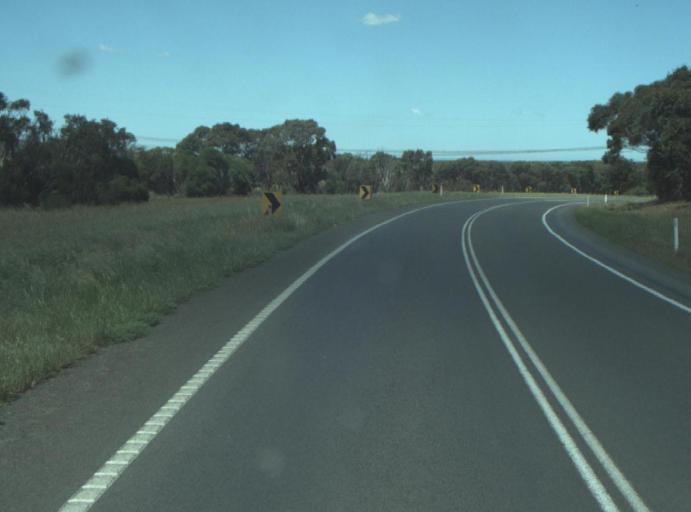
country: AU
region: Victoria
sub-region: Greater Geelong
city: Lara
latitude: -37.9017
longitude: 144.3709
